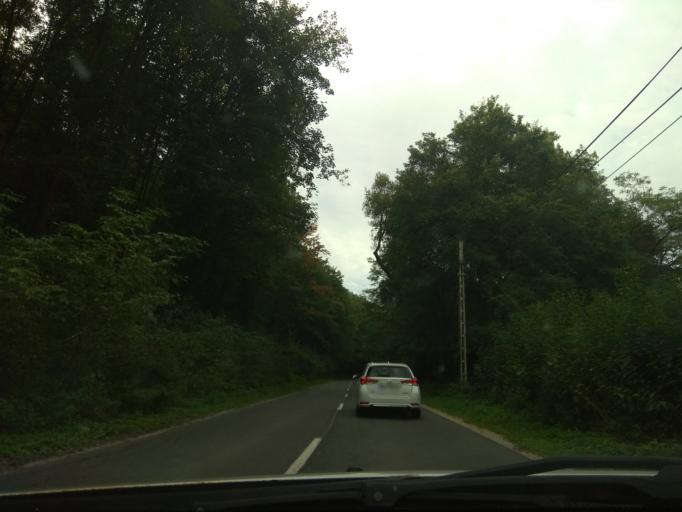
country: HU
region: Borsod-Abauj-Zemplen
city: Miskolc
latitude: 48.0821
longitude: 20.7001
